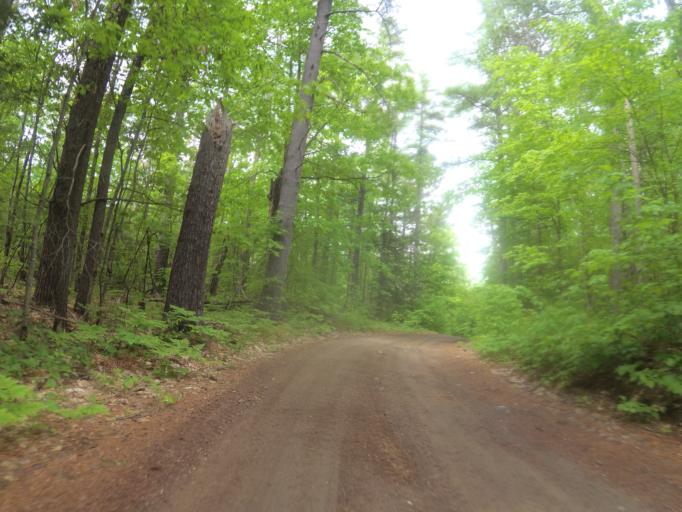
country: CA
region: Ontario
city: Renfrew
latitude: 45.1095
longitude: -76.8238
